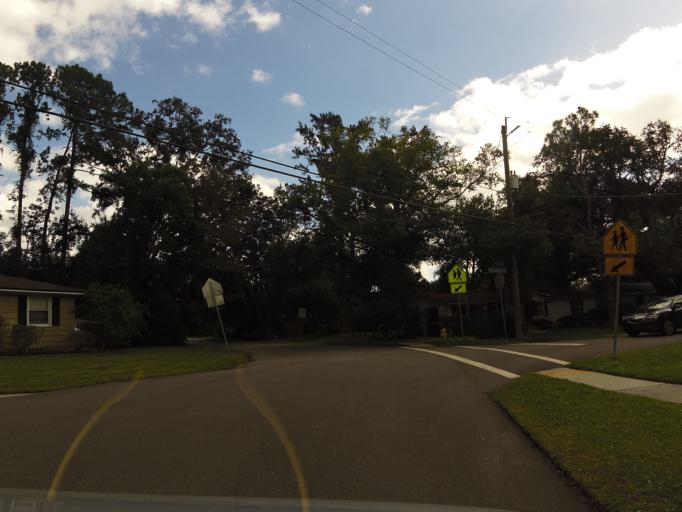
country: US
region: Florida
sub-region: Duval County
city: Jacksonville
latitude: 30.2632
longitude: -81.7062
